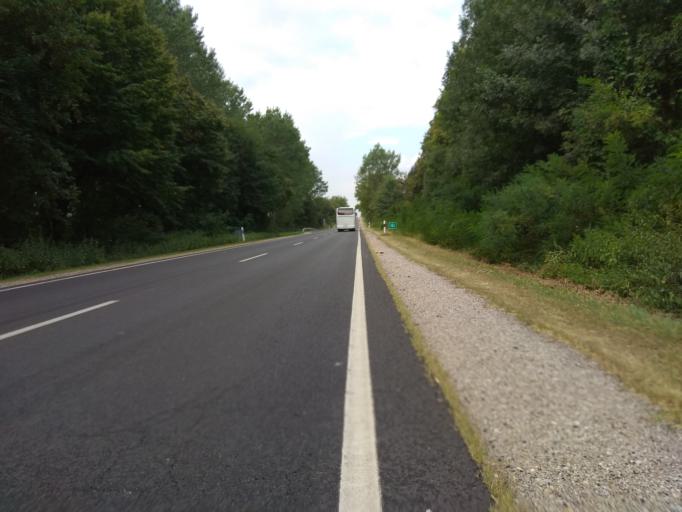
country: HU
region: Borsod-Abauj-Zemplen
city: Emod
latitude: 47.9268
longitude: 20.7783
